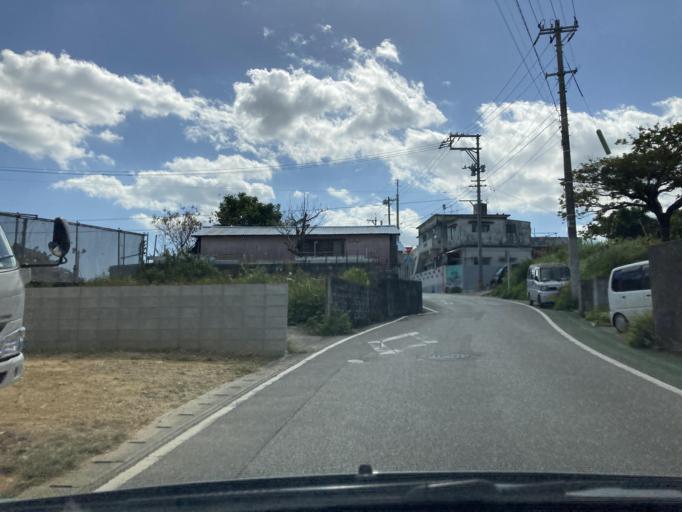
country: JP
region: Okinawa
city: Okinawa
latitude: 26.3431
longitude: 127.8030
